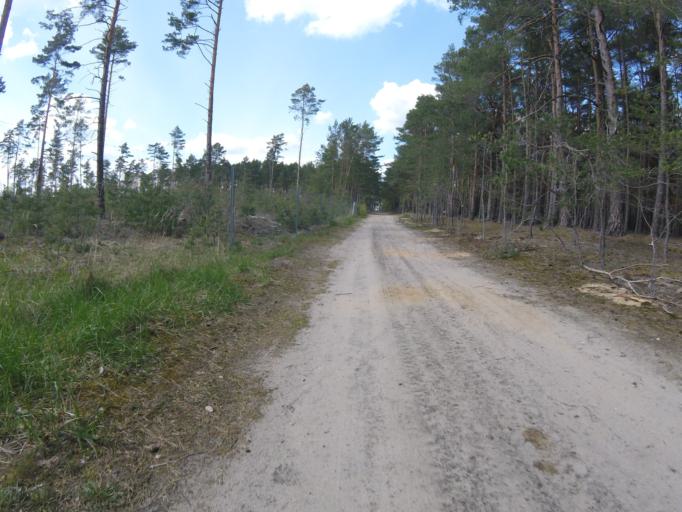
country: DE
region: Brandenburg
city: Bestensee
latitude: 52.2194
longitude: 13.6572
